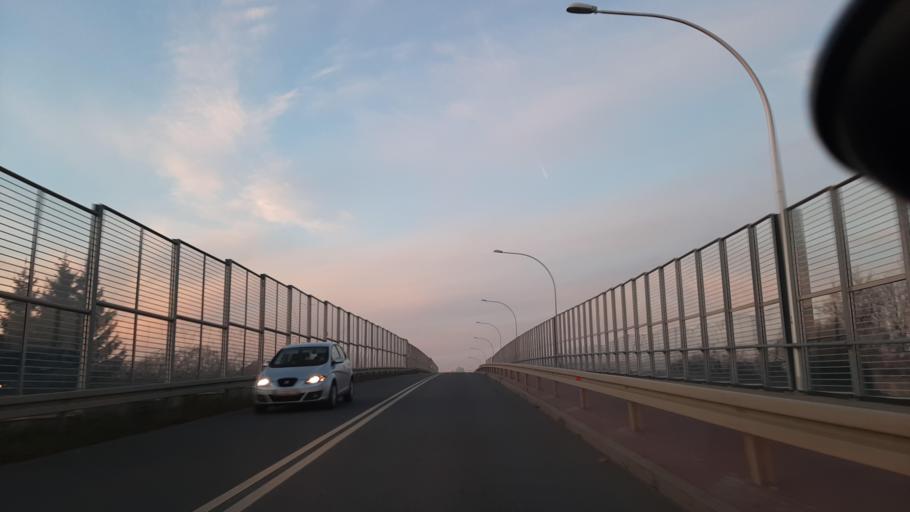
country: PL
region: Lublin Voivodeship
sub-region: Powiat lubelski
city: Jastkow
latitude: 51.2999
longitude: 22.4930
